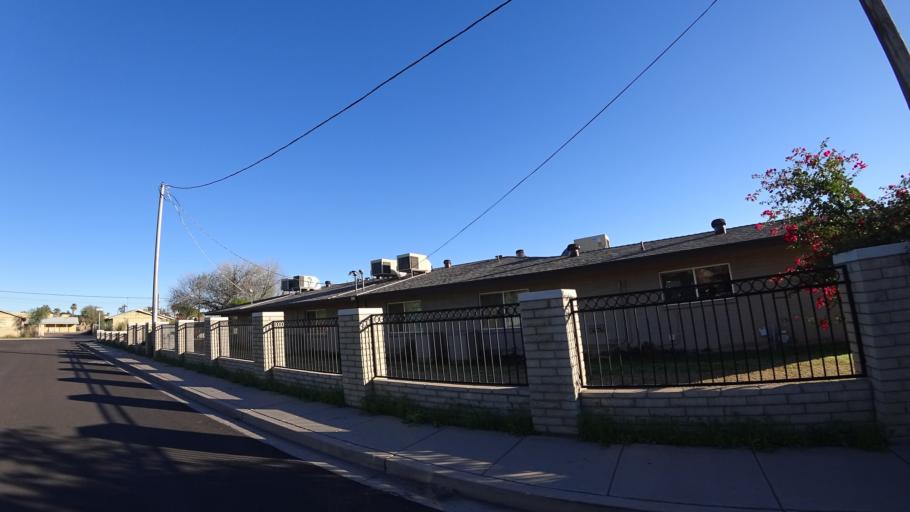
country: US
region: Arizona
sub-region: Maricopa County
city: Phoenix
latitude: 33.4861
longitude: -112.0444
